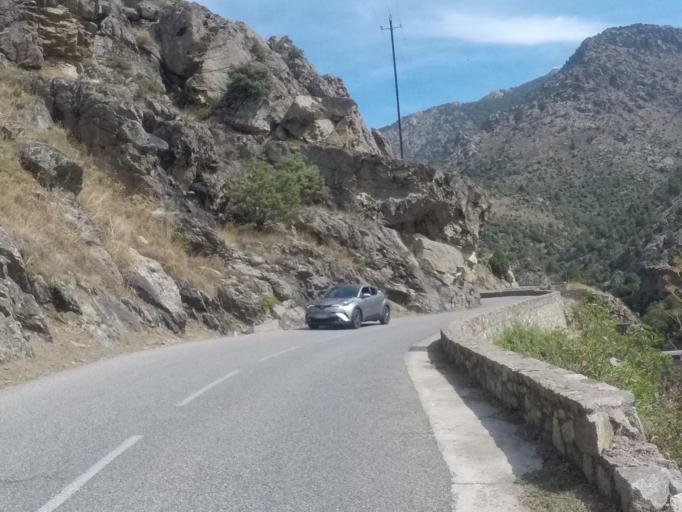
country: FR
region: Corsica
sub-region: Departement de la Haute-Corse
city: Corte
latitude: 42.3437
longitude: 9.0455
